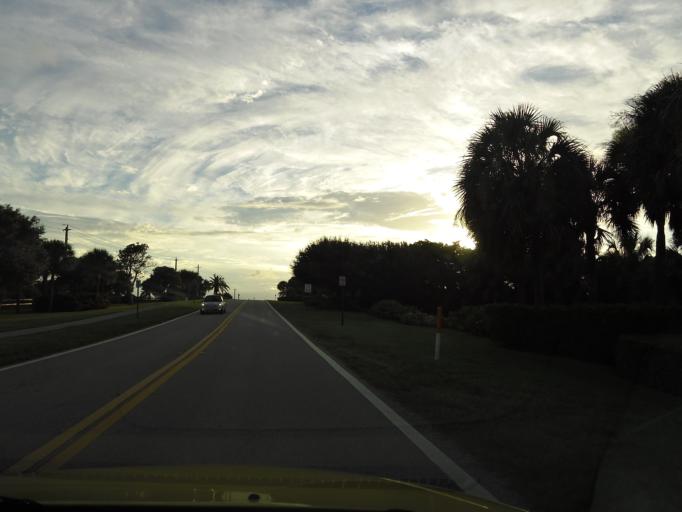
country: US
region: Florida
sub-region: Palm Beach County
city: Jupiter
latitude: 26.9526
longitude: -80.0806
